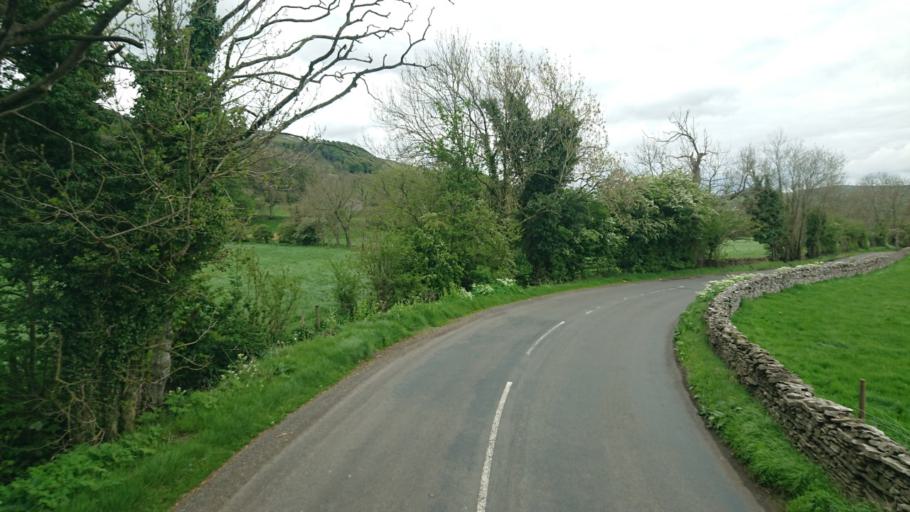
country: GB
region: England
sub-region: North Yorkshire
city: Leyburn
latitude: 54.2891
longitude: -1.9661
